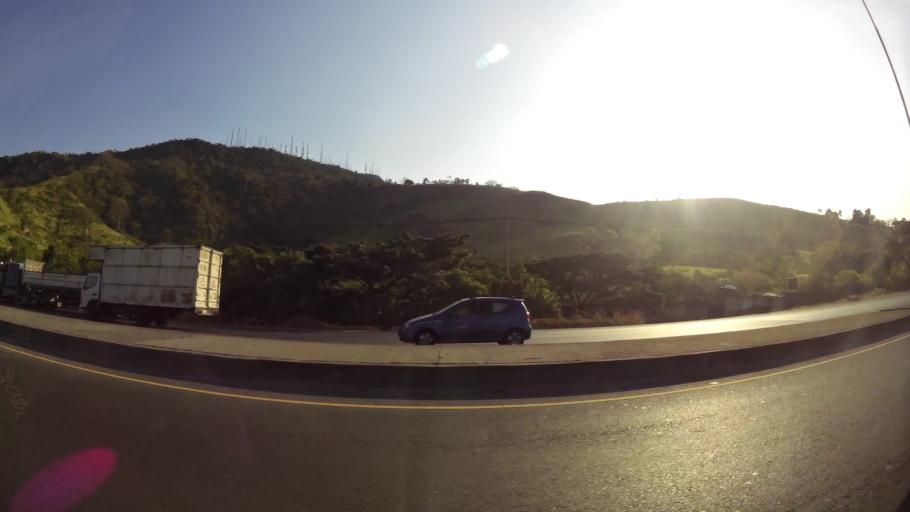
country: EC
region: Guayas
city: Santa Lucia
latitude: -2.1613
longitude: -79.9488
